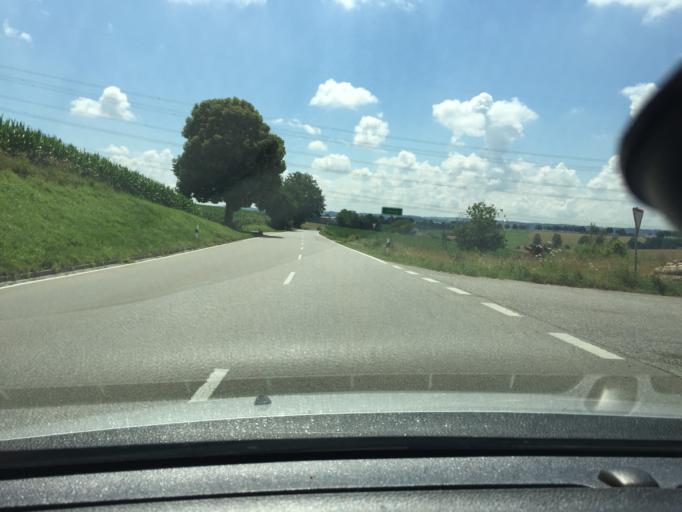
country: DE
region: Bavaria
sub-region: Upper Bavaria
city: Dorfen
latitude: 48.2991
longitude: 12.1215
